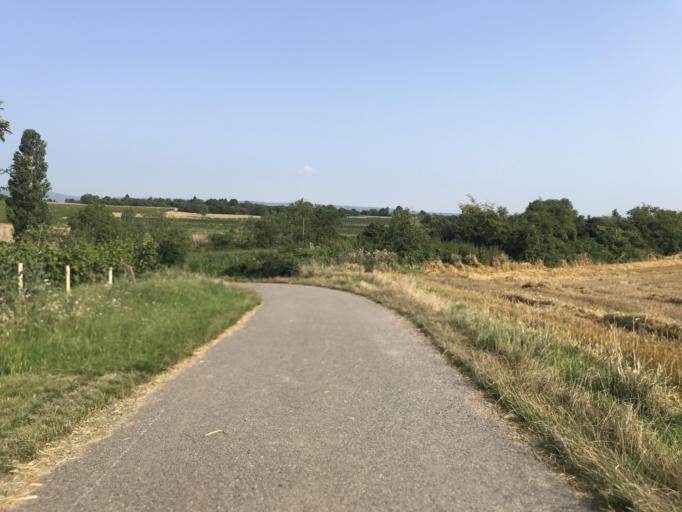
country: DE
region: Hesse
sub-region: Regierungsbezirk Darmstadt
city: Hochheim am Main
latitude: 50.0142
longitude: 8.3230
